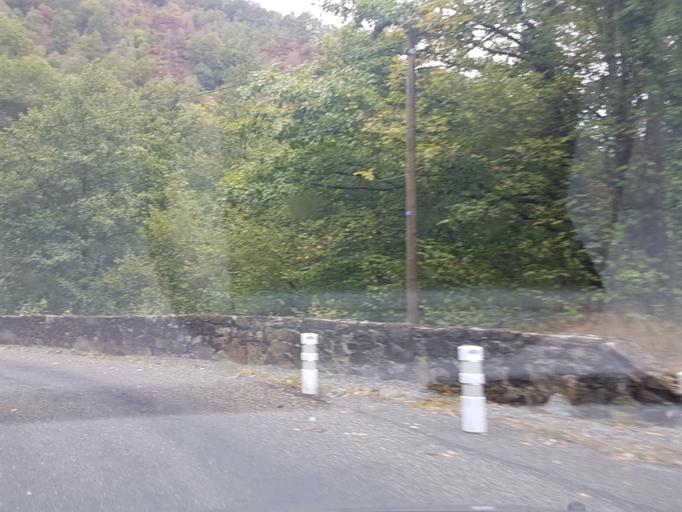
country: FR
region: Midi-Pyrenees
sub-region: Departement de l'Ariege
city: Saint-Girons
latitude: 42.9086
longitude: 1.2737
